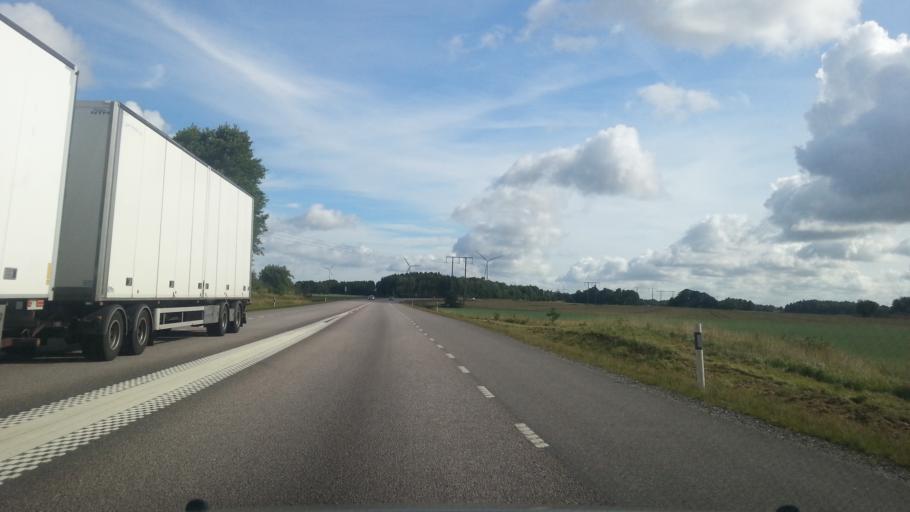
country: SE
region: Vaestra Goetaland
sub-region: Grastorps Kommun
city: Graestorp
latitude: 58.3154
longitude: 12.5630
